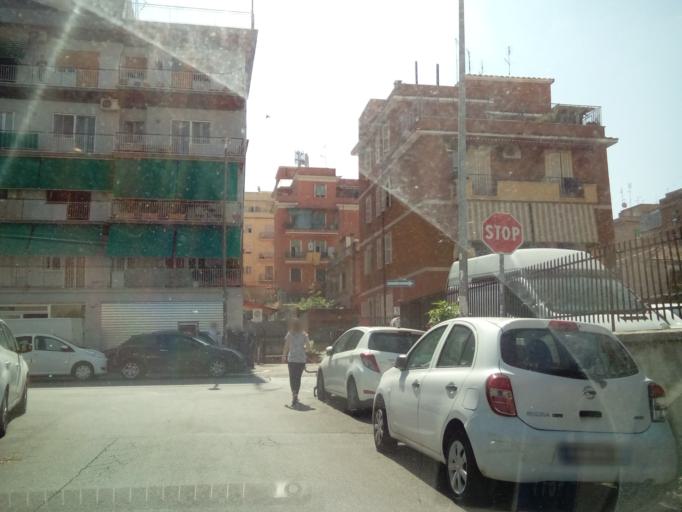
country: IT
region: Latium
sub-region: Citta metropolitana di Roma Capitale
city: Rome
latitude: 41.8739
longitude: 12.5733
